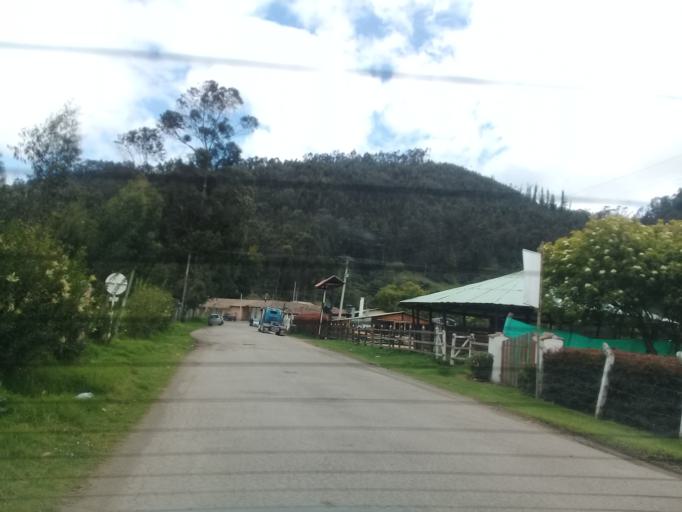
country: CO
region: Cundinamarca
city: Tenjo
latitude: 4.8573
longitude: -74.1942
